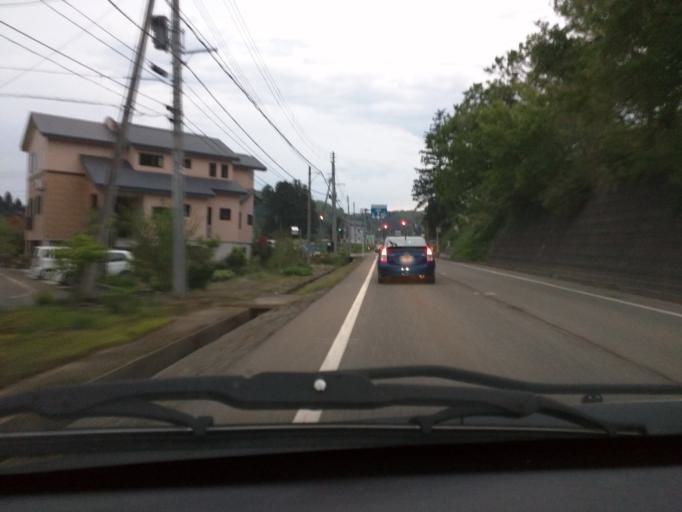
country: JP
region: Niigata
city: Ojiya
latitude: 37.3227
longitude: 138.7110
